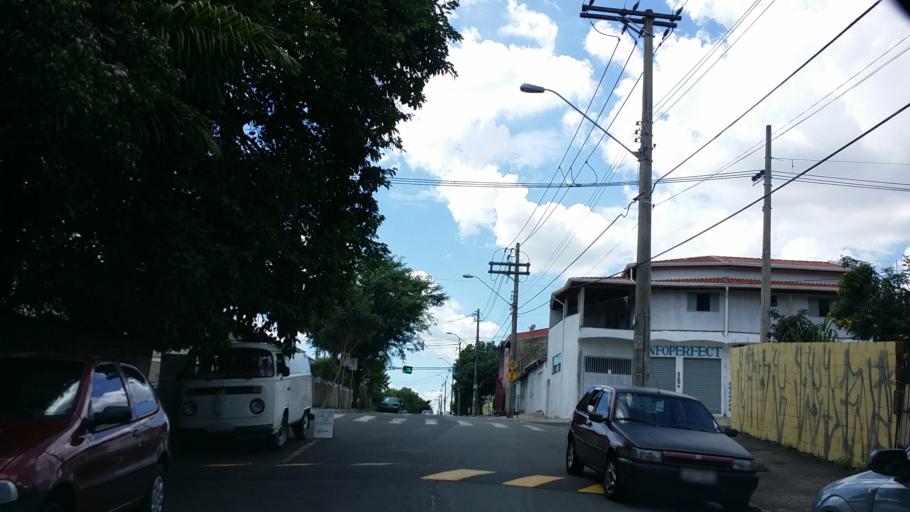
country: BR
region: Sao Paulo
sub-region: Indaiatuba
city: Indaiatuba
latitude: -23.1219
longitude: -47.2465
